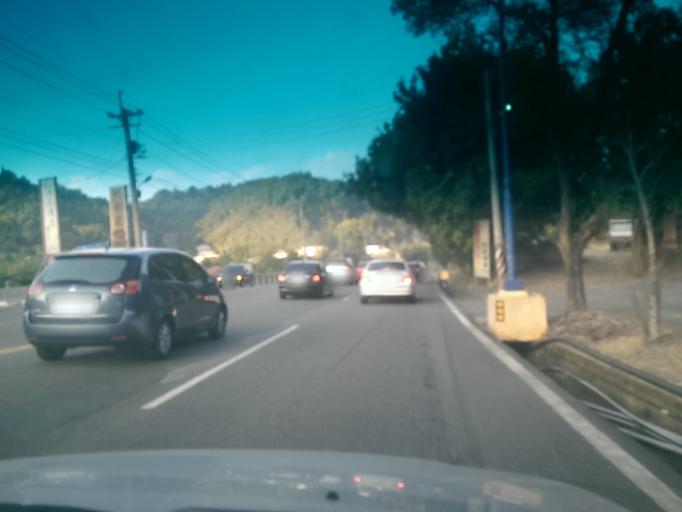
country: TW
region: Taiwan
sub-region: Nantou
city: Puli
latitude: 23.9409
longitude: 120.9279
